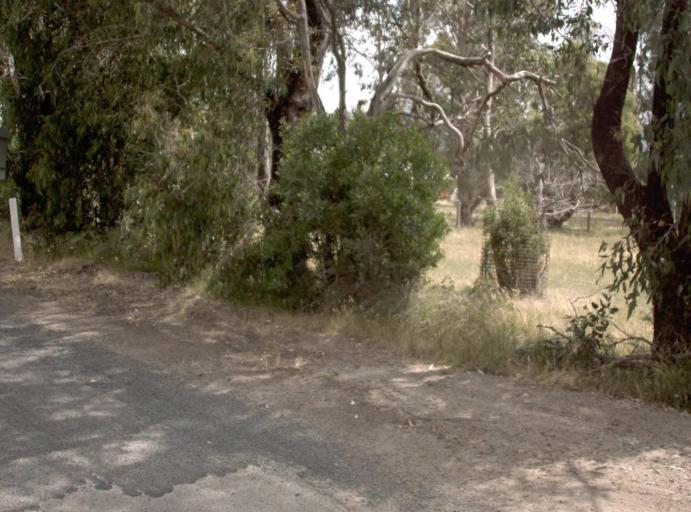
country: AU
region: Victoria
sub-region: Latrobe
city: Traralgon
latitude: -38.3148
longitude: 146.5669
